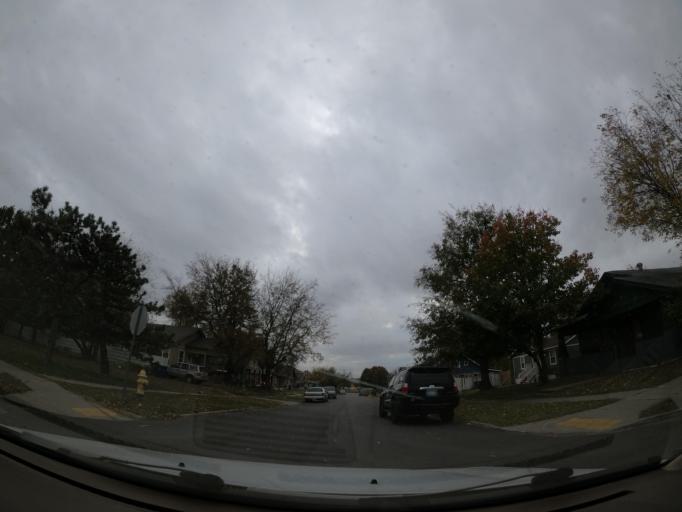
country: US
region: Oklahoma
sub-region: Tulsa County
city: Tulsa
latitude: 36.1626
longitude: -95.9621
